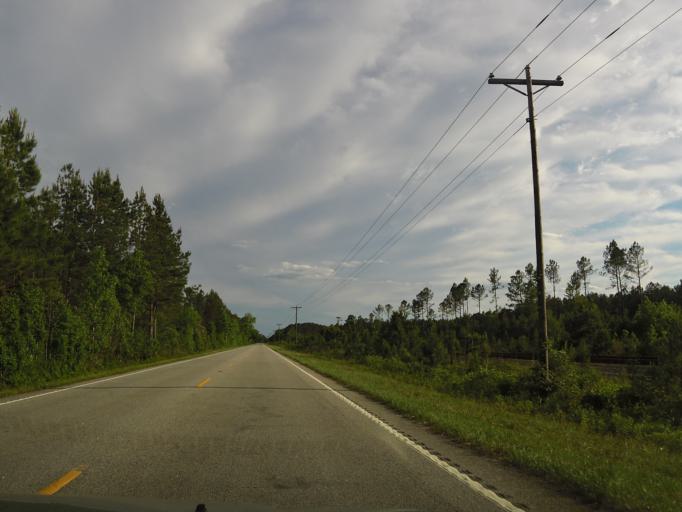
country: US
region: South Carolina
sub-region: Hampton County
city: Estill
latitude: 32.6249
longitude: -81.2444
